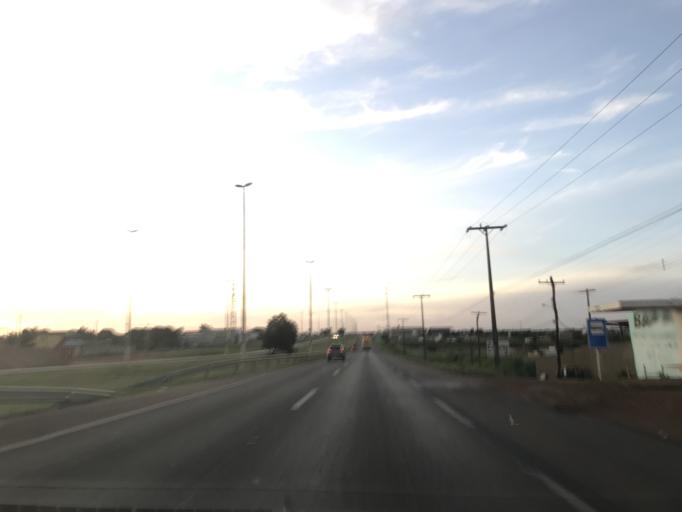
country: BR
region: Goias
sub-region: Luziania
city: Luziania
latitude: -16.2294
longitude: -47.9140
